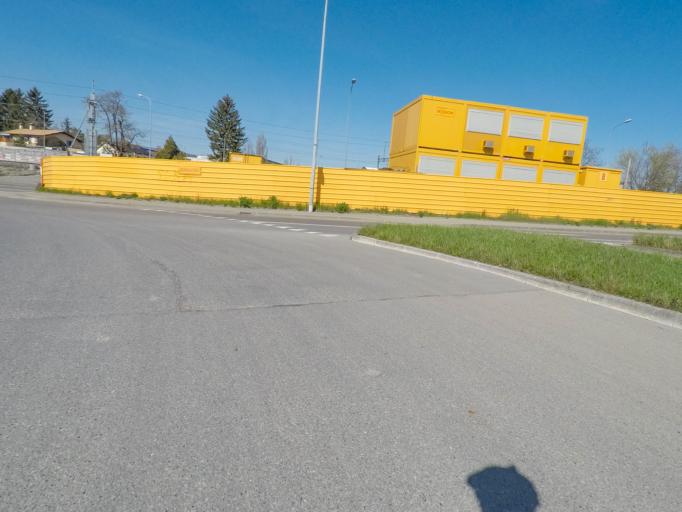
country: CH
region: Geneva
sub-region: Geneva
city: Vernier
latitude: 46.2216
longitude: 6.0763
